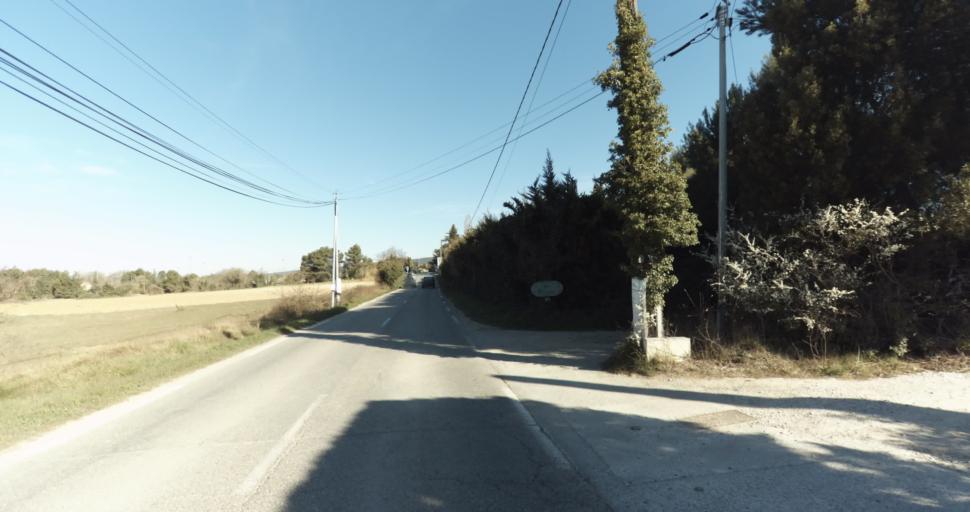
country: FR
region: Provence-Alpes-Cote d'Azur
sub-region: Departement des Bouches-du-Rhone
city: Aix-en-Provence
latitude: 43.5717
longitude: 5.4240
